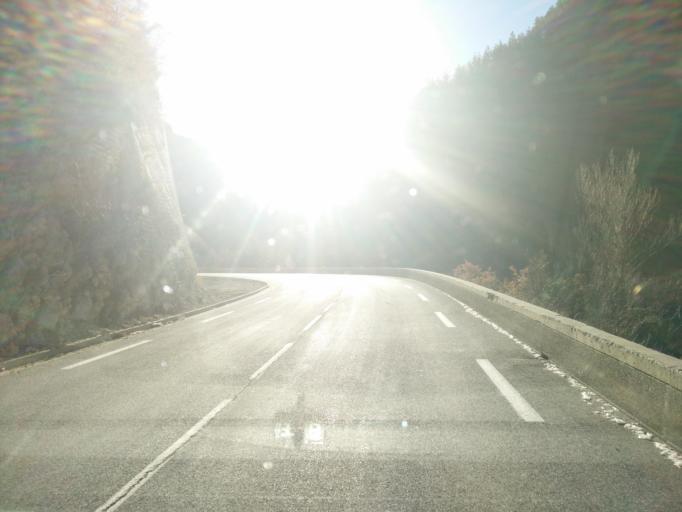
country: FR
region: Provence-Alpes-Cote d'Azur
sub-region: Departement des Alpes-de-Haute-Provence
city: Annot
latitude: 43.9527
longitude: 6.6852
